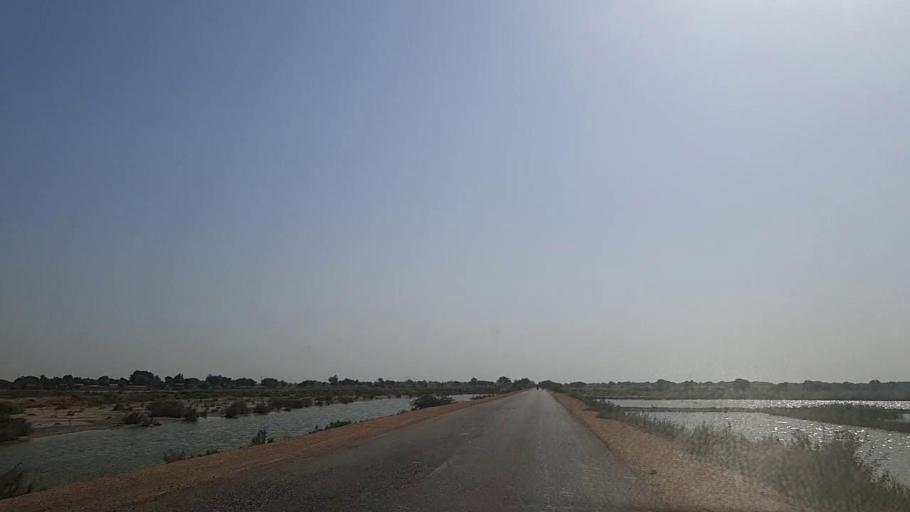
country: PK
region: Sindh
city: Mirpur Batoro
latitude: 24.5806
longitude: 68.2892
